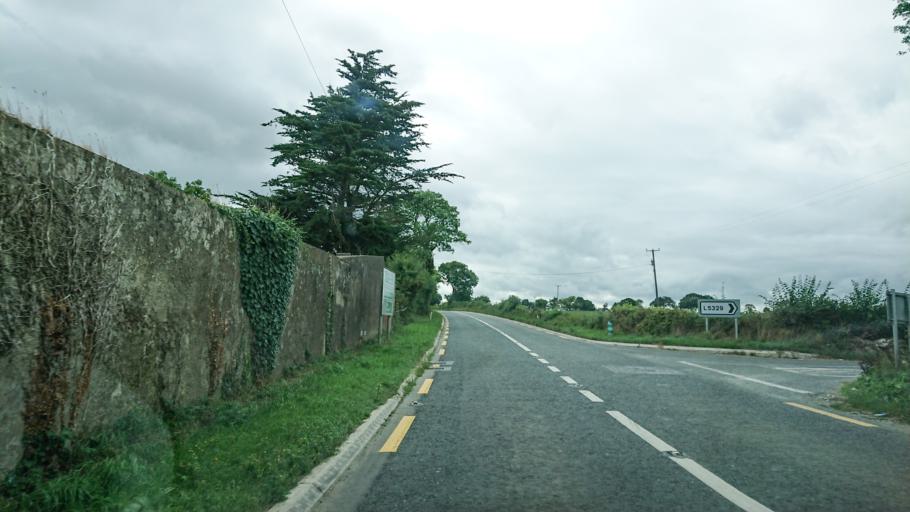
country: IE
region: Munster
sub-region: County Cork
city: Mallow
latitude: 52.1546
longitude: -8.5782
